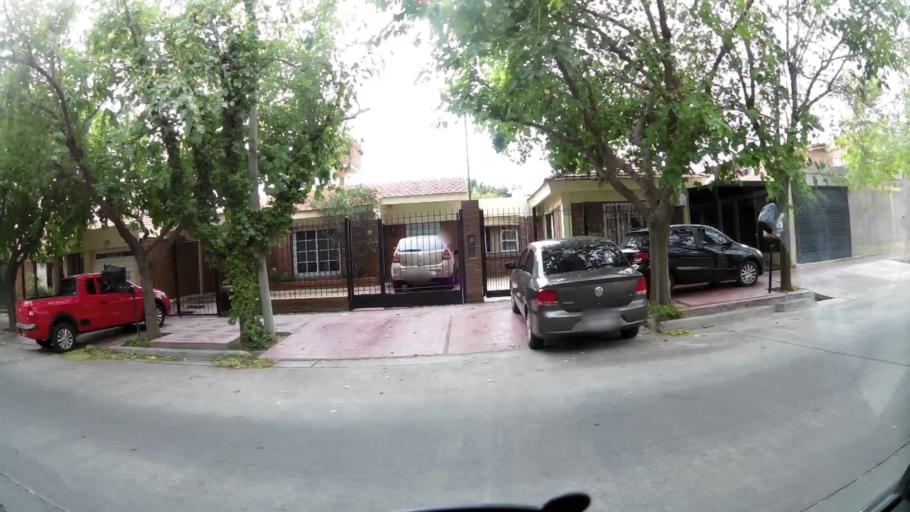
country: AR
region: Mendoza
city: Las Heras
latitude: -32.8594
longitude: -68.8547
